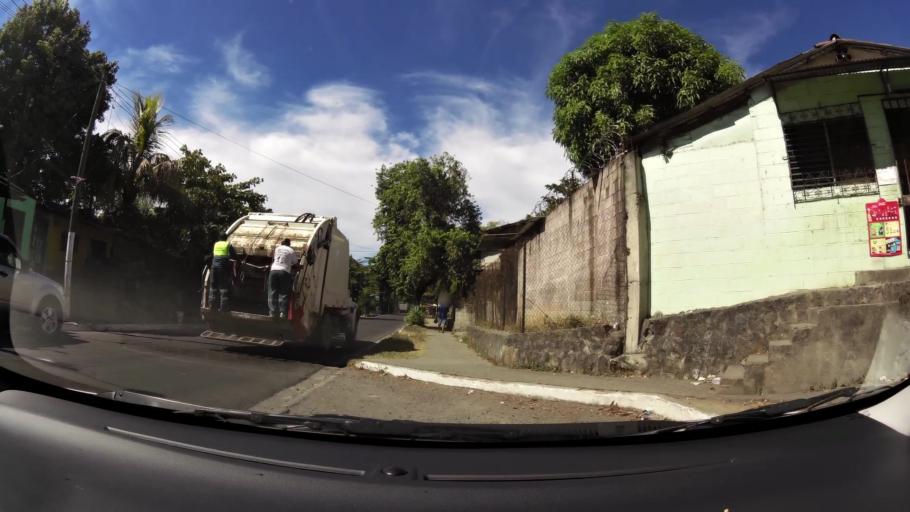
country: SV
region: San Salvador
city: Apopa
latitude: 13.8057
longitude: -89.1801
